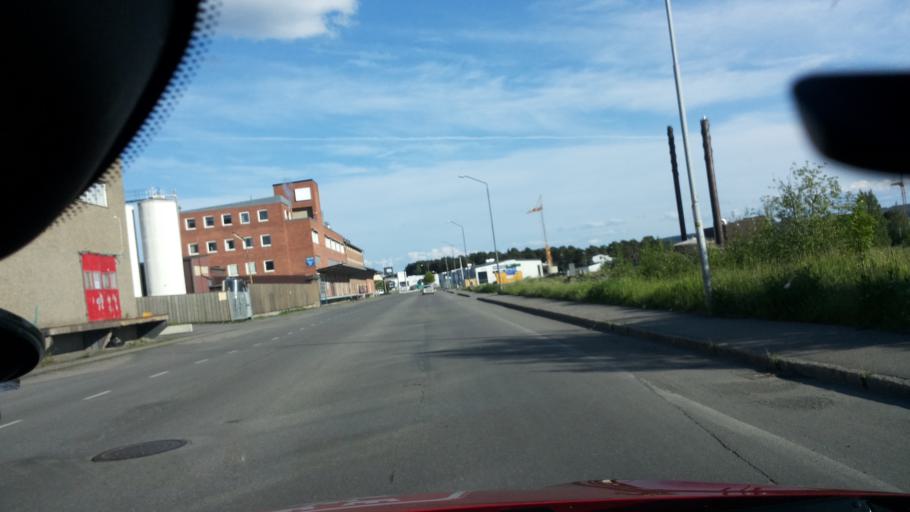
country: SE
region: Jaemtland
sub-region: OEstersunds Kommun
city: Ostersund
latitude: 63.1661
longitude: 14.6462
